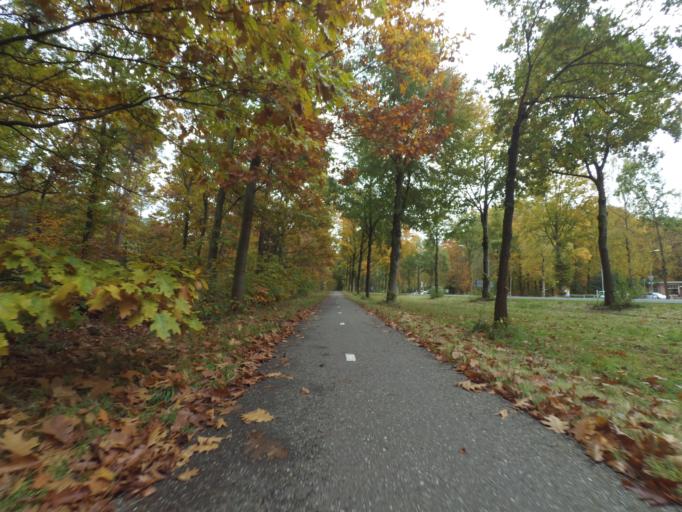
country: NL
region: Gelderland
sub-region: Gemeente Ermelo
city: Ermelo
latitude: 52.3025
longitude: 5.6494
